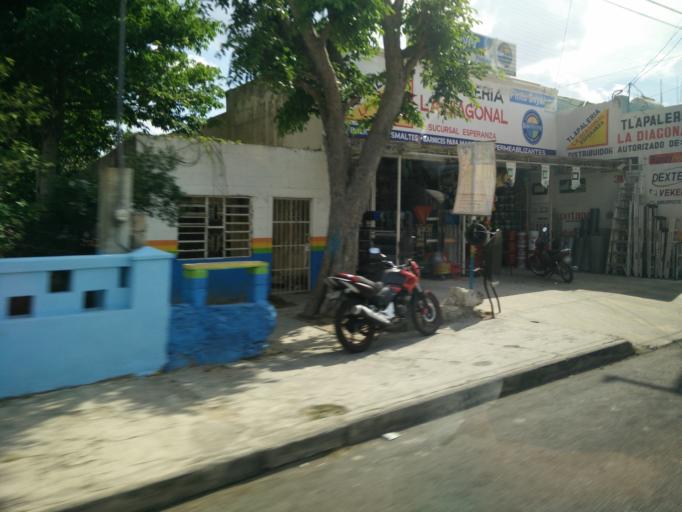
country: MX
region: Yucatan
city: Merida
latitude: 20.9645
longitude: -89.5937
